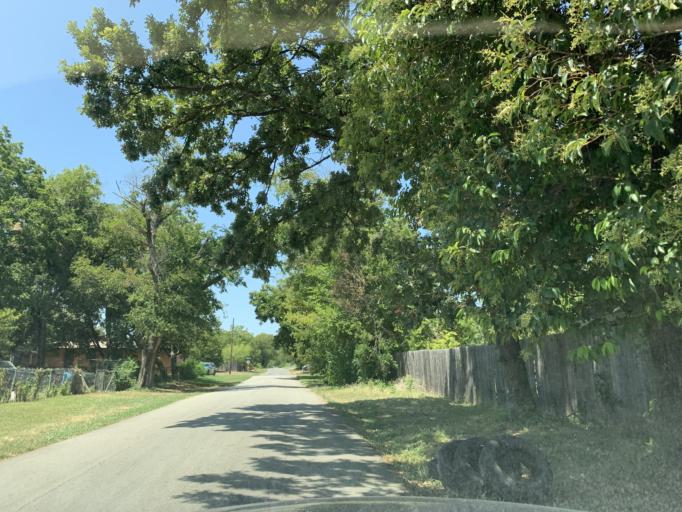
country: US
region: Texas
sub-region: Dallas County
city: Hutchins
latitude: 32.6858
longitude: -96.8021
